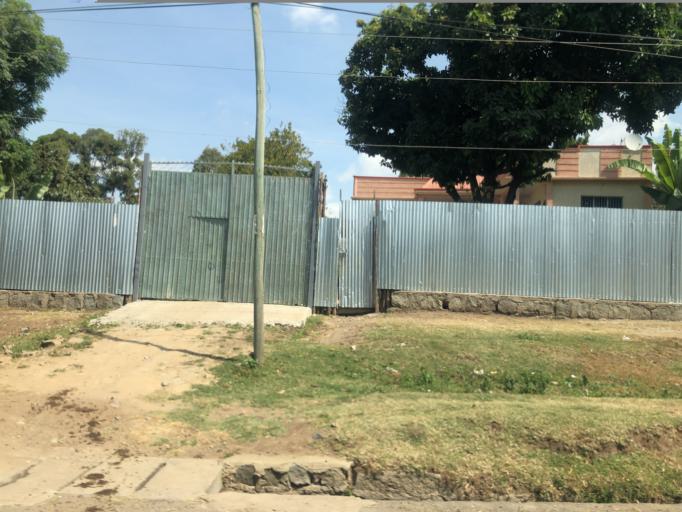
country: ET
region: Oromiya
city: Shashemene
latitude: 7.2695
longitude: 38.6561
